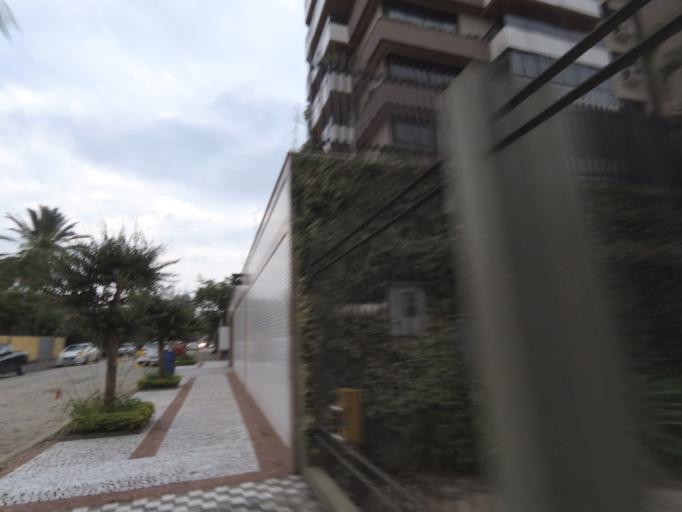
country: BR
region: Santa Catarina
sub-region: Blumenau
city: Blumenau
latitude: -26.9192
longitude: -49.0626
